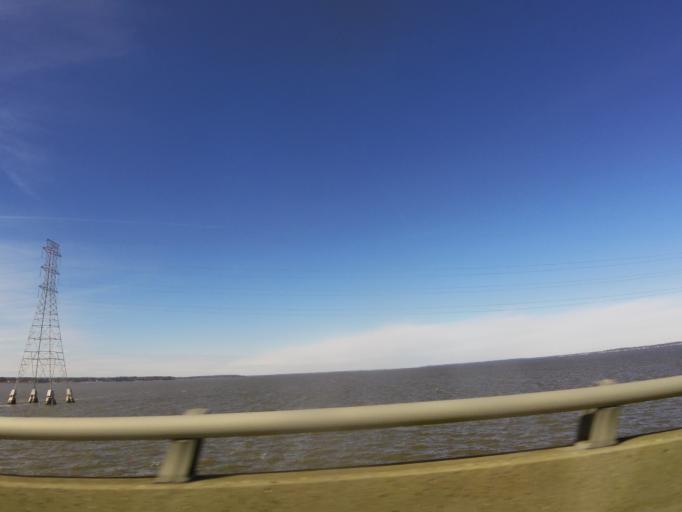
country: US
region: Virginia
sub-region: Isle of Wight County
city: Carrollton
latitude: 36.9768
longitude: -76.5008
